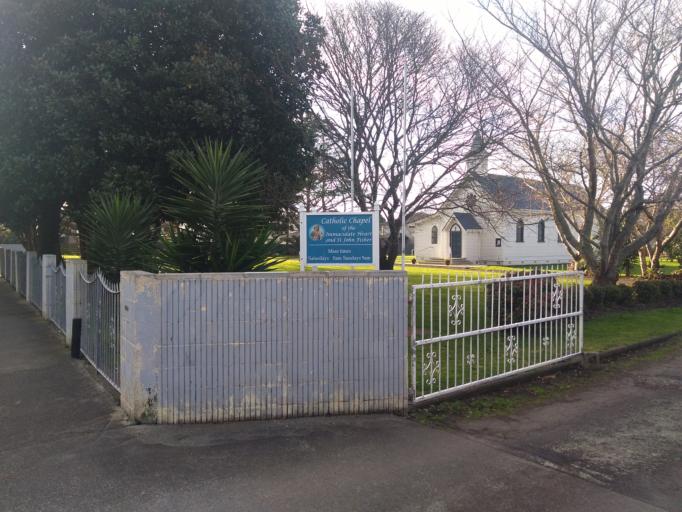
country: NZ
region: Auckland
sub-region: Auckland
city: Rosebank
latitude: -36.8897
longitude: 174.6777
